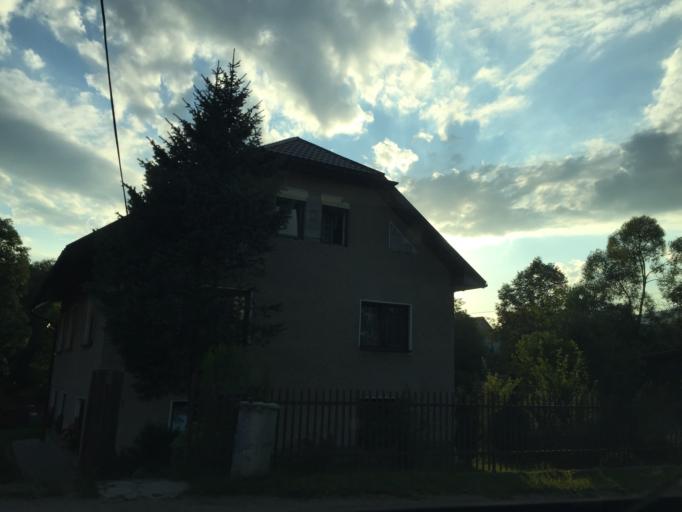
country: PL
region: Silesian Voivodeship
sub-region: Powiat zywiecki
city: Korbielow
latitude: 49.4789
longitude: 19.3828
